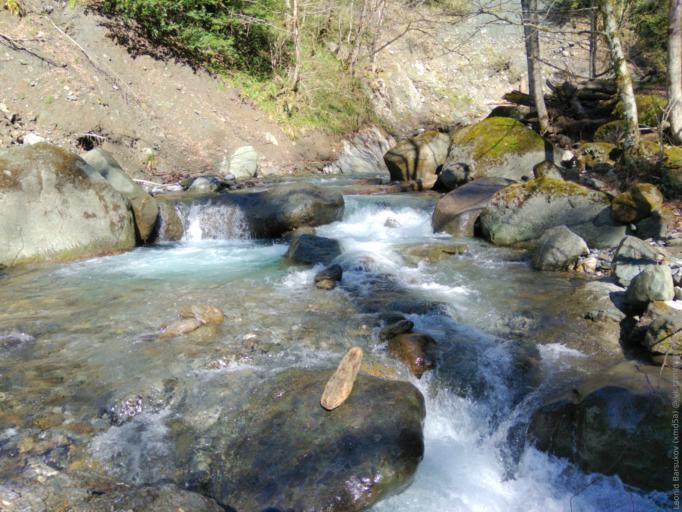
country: RU
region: Krasnodarskiy
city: Dagomys
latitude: 43.7631
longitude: 39.8220
